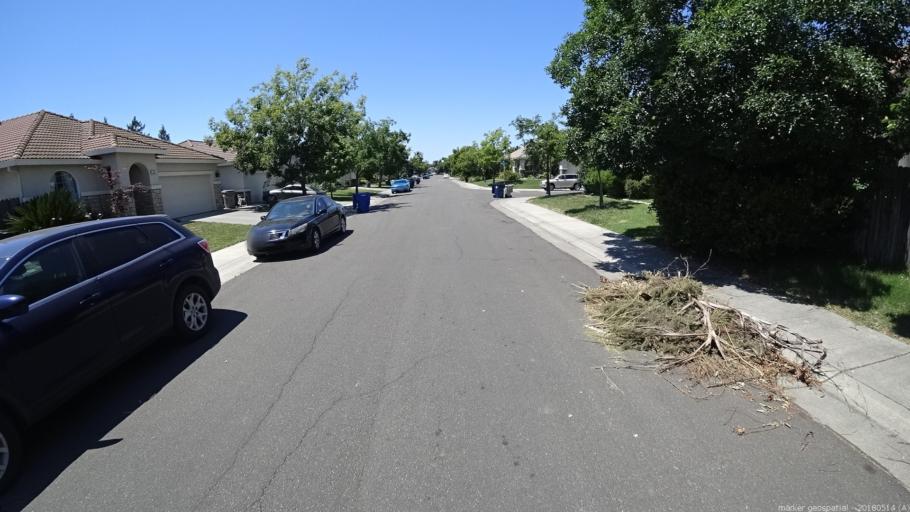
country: US
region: California
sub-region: Yolo County
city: West Sacramento
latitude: 38.6278
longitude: -121.5359
